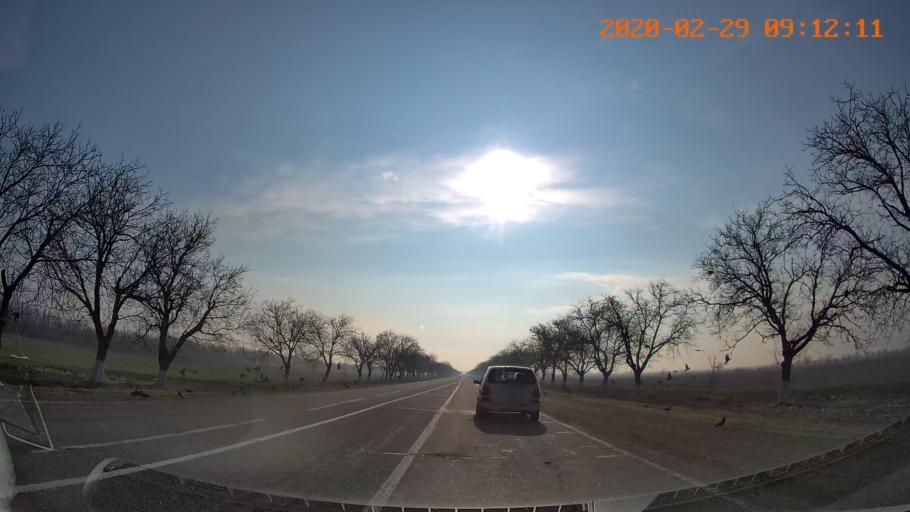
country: MD
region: Telenesti
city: Slobozia
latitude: 46.8289
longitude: 29.8124
